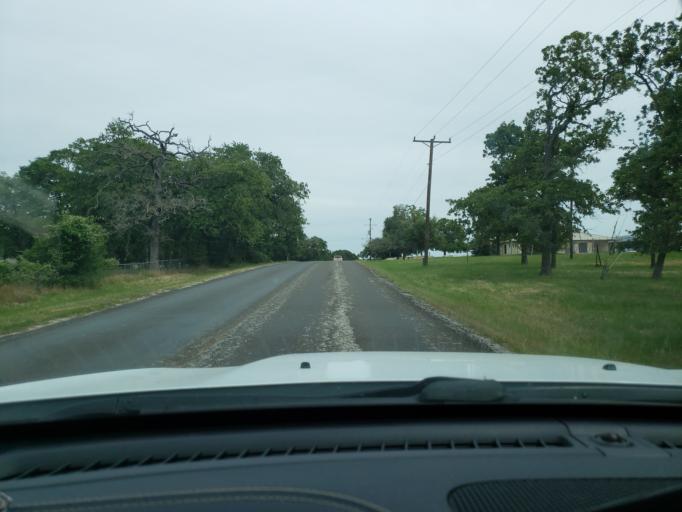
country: US
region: Texas
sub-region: Burleson County
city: Somerville
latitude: 30.3376
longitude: -96.5412
